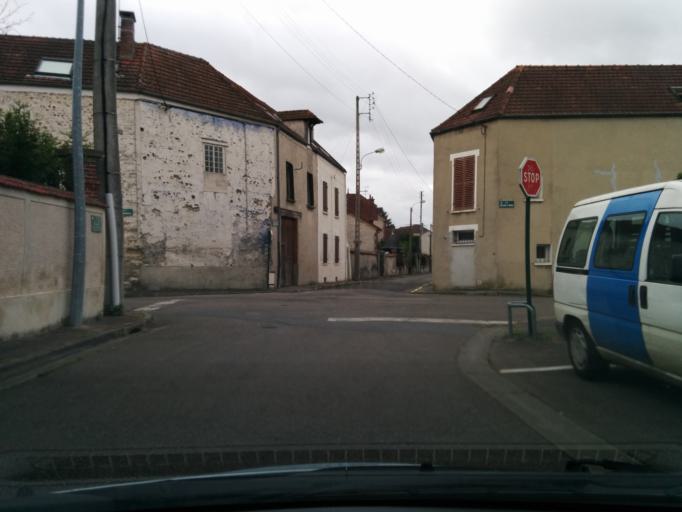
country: FR
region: Ile-de-France
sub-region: Departement des Yvelines
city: Limay
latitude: 48.9963
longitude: 1.7272
